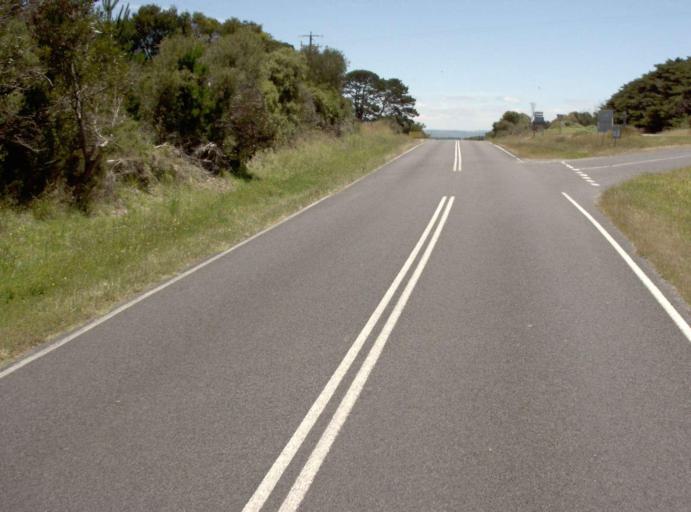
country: AU
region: Victoria
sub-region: Latrobe
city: Morwell
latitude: -38.8367
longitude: 146.2414
